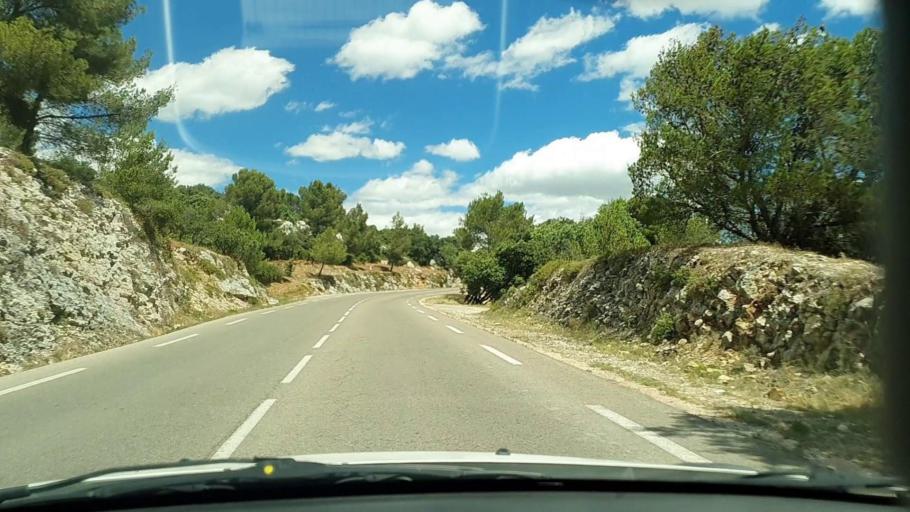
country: FR
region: Languedoc-Roussillon
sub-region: Departement du Gard
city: Poulx
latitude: 43.8949
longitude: 4.4209
